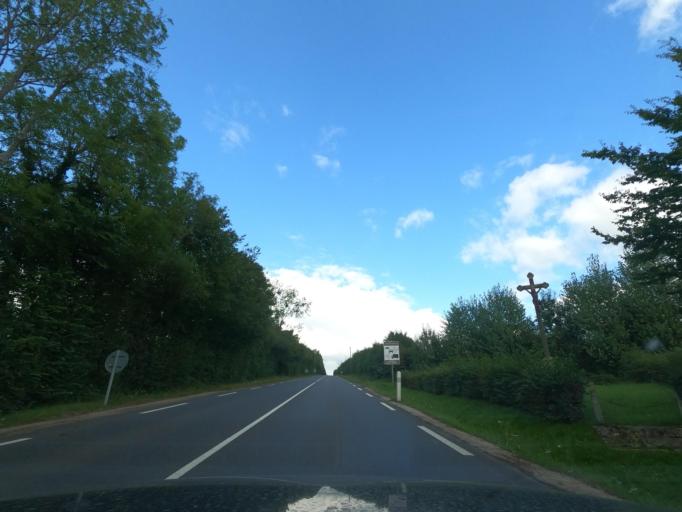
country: FR
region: Lower Normandy
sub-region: Departement de l'Orne
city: Gace
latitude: 48.8136
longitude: 0.3105
